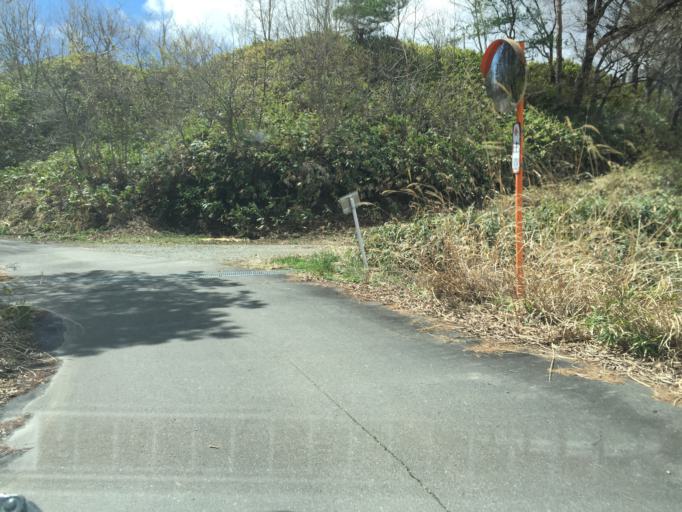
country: JP
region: Fukushima
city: Fukushima-shi
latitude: 37.8453
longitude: 140.4309
